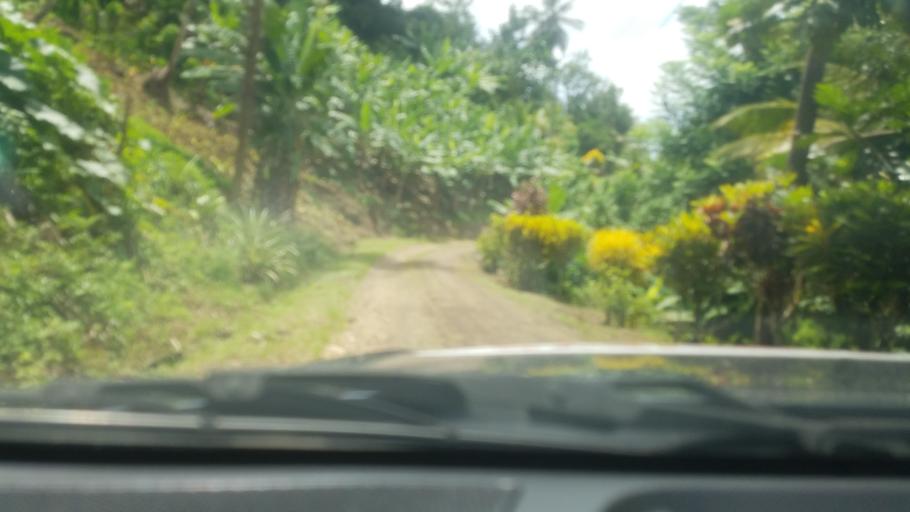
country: LC
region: Micoud Quarter
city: Micoud
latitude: 13.8026
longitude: -60.9514
